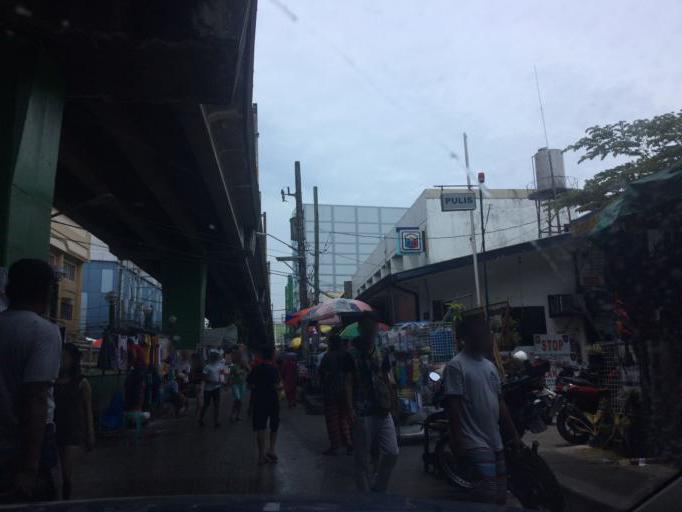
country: PH
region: Metro Manila
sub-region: Makati City
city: Makati City
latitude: 14.5352
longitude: 120.9991
